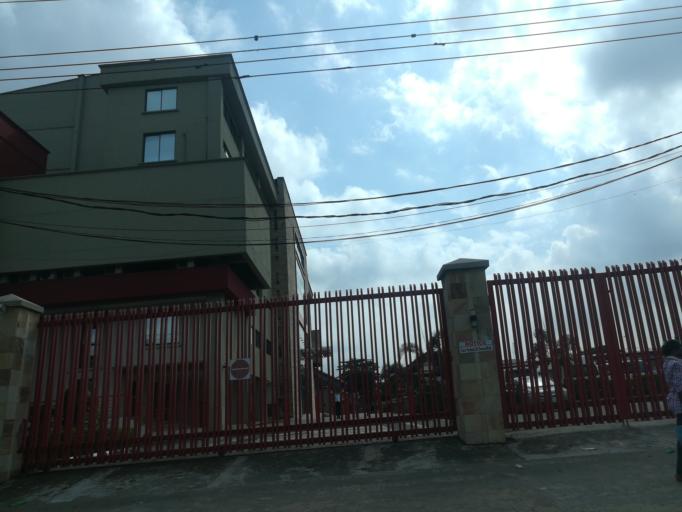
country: NG
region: Lagos
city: Oshodi
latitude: 6.5529
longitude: 3.3550
